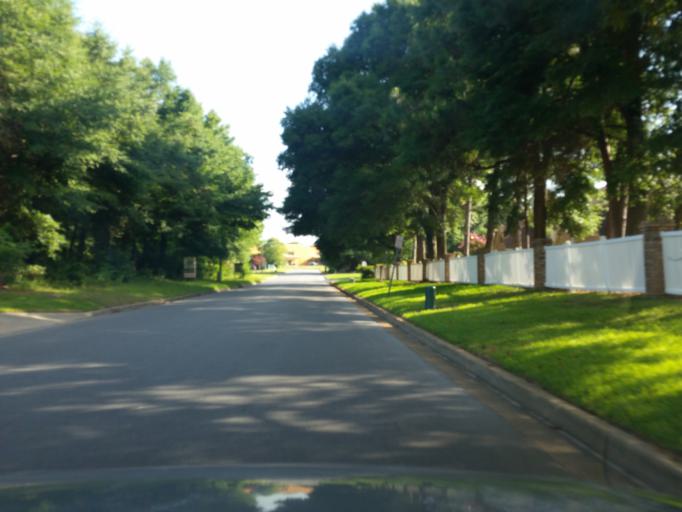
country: US
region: Florida
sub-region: Escambia County
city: Brent
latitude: 30.4719
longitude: -87.2038
